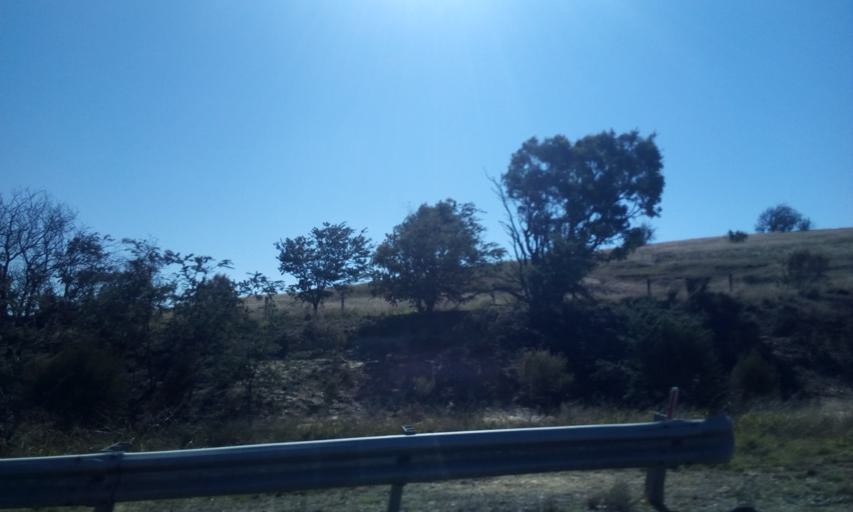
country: AU
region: New South Wales
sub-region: Goulburn Mulwaree
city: Goulburn
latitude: -34.7798
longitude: 149.6720
